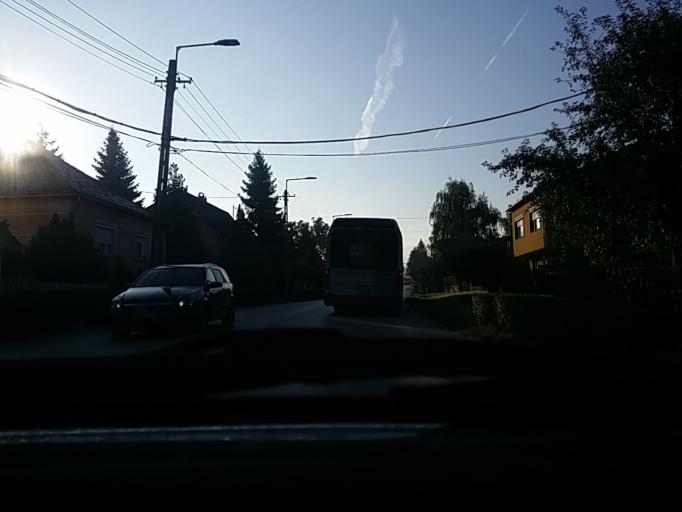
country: HU
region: Komarom-Esztergom
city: Pilismarot
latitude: 47.7823
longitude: 18.8825
